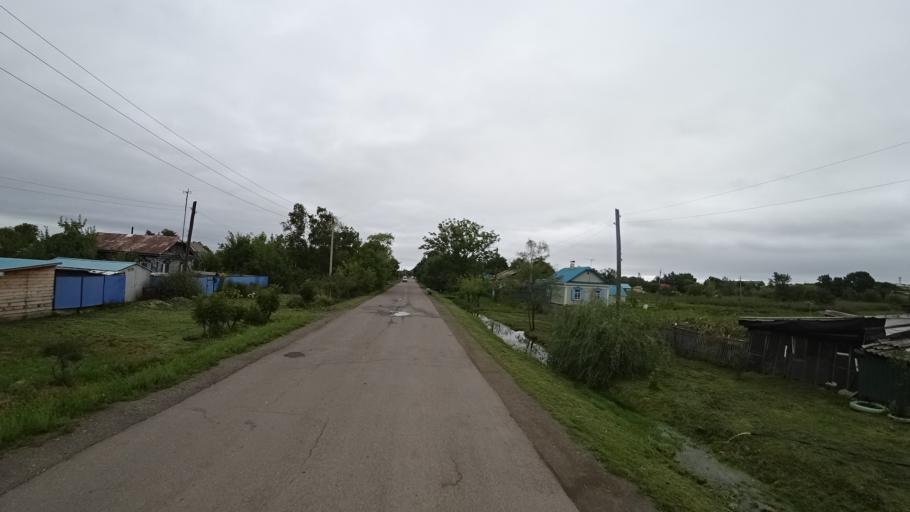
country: RU
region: Primorskiy
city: Chernigovka
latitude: 44.3475
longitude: 132.5640
